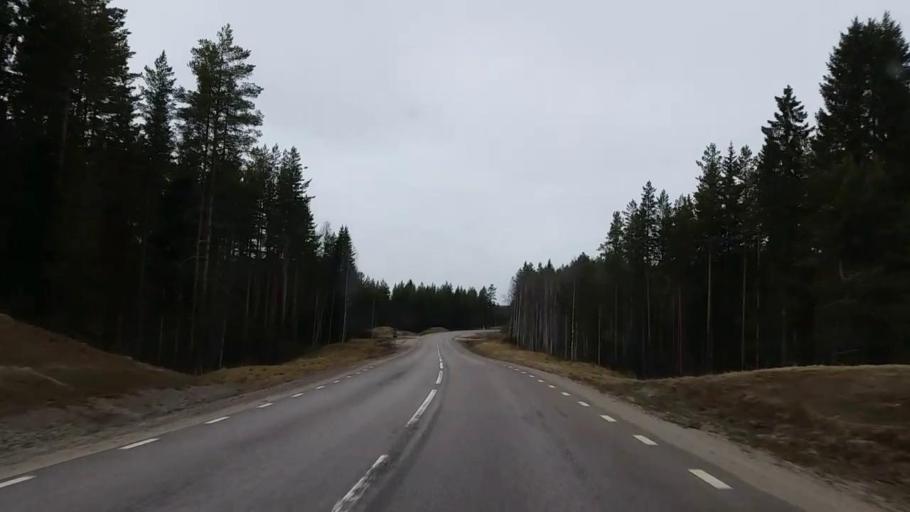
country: SE
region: Gaevleborg
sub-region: Ovanakers Kommun
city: Edsbyn
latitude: 61.1768
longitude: 15.8823
